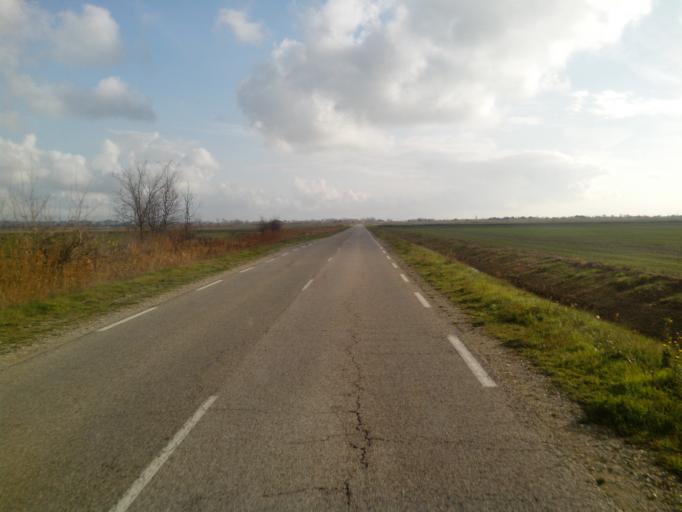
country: FR
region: Provence-Alpes-Cote d'Azur
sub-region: Departement des Bouches-du-Rhone
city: Port-Saint-Louis-du-Rhone
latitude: 43.4613
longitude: 4.7172
